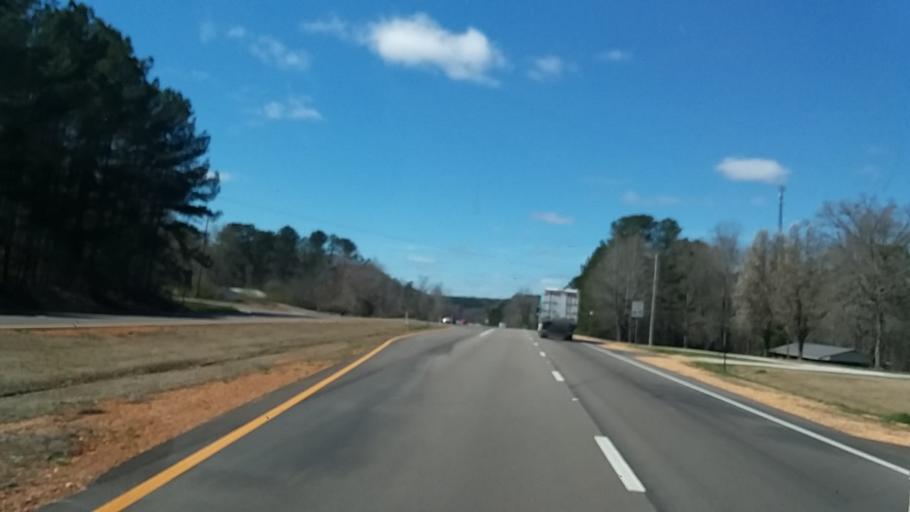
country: US
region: Mississippi
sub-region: Tishomingo County
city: Iuka
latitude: 34.8455
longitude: -88.3313
